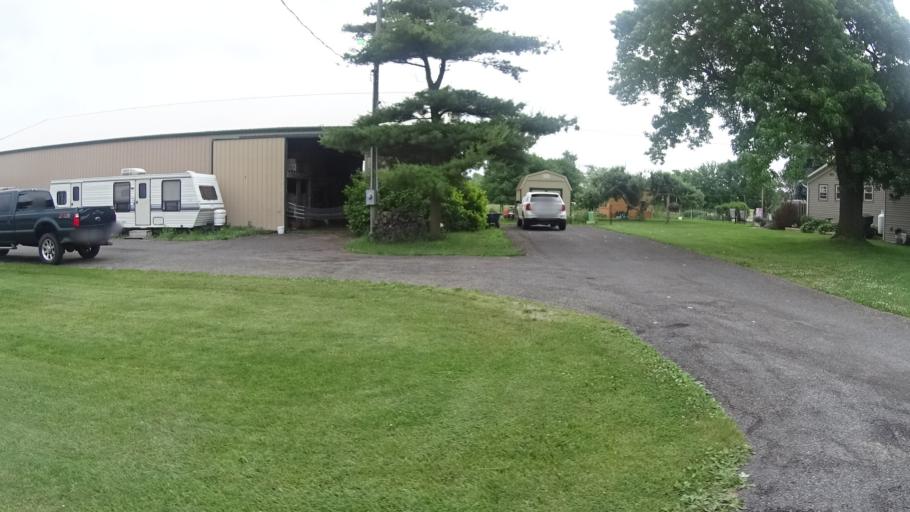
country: US
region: Ohio
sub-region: Huron County
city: Bellevue
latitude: 41.3430
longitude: -82.7940
